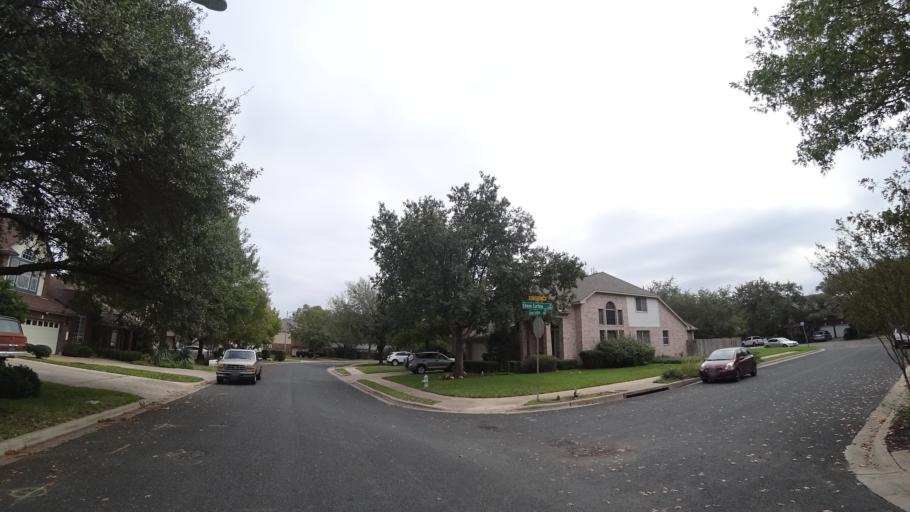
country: US
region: Texas
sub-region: Travis County
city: Shady Hollow
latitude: 30.2220
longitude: -97.8747
